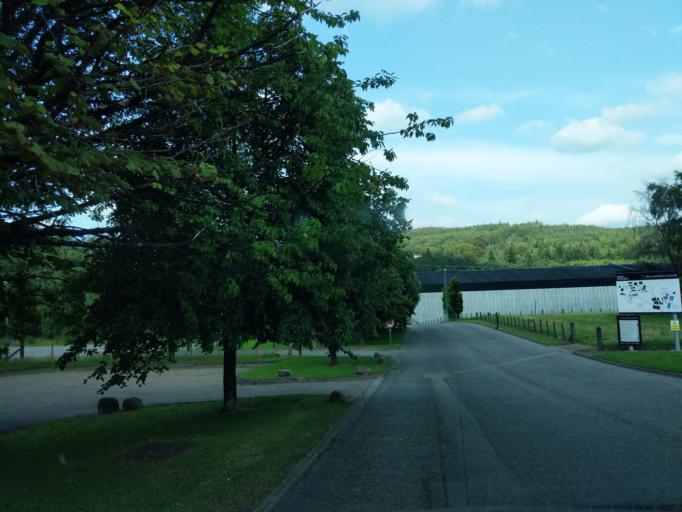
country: GB
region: Scotland
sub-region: Moray
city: Dufftown
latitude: 57.4599
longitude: -3.1323
